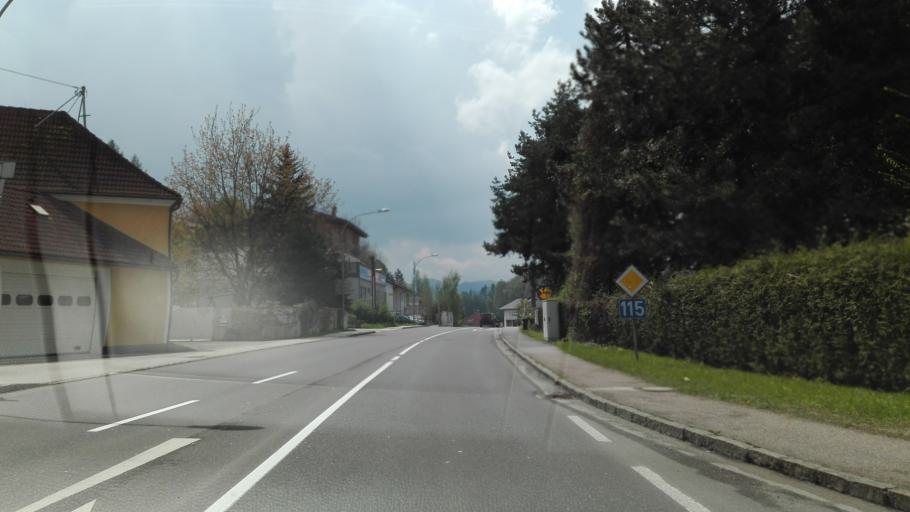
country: AT
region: Upper Austria
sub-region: Politischer Bezirk Steyr-Land
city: Sankt Ulrich bei Steyr
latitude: 48.0269
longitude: 14.4187
